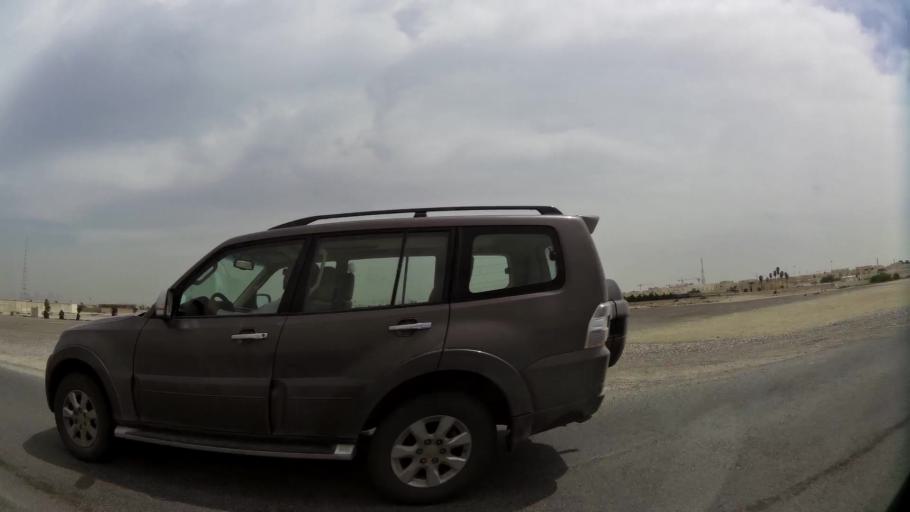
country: QA
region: Baladiyat ar Rayyan
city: Ar Rayyan
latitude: 25.2744
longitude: 51.4607
